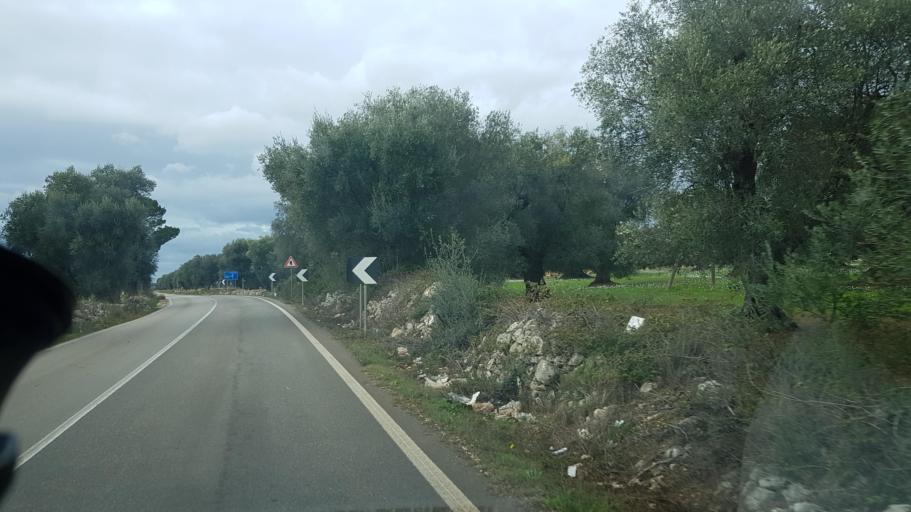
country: IT
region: Apulia
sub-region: Provincia di Brindisi
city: Francavilla Fontana
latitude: 40.5486
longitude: 17.5411
